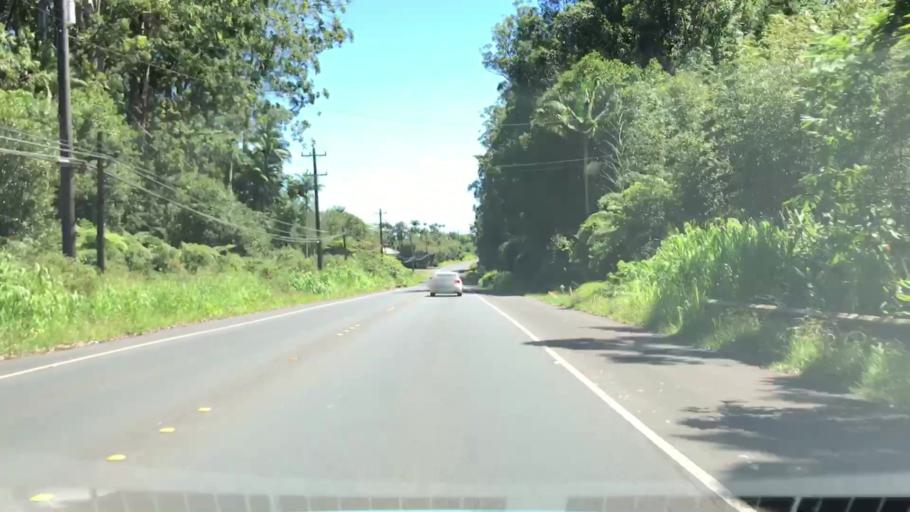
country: US
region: Hawaii
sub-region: Hawaii County
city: Mountain View
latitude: 19.5453
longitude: -155.1146
